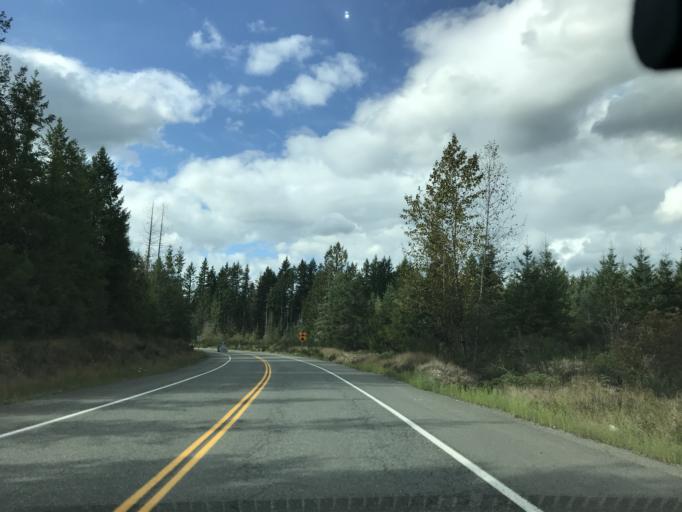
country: US
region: Washington
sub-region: King County
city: Black Diamond
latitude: 47.2993
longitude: -122.0505
